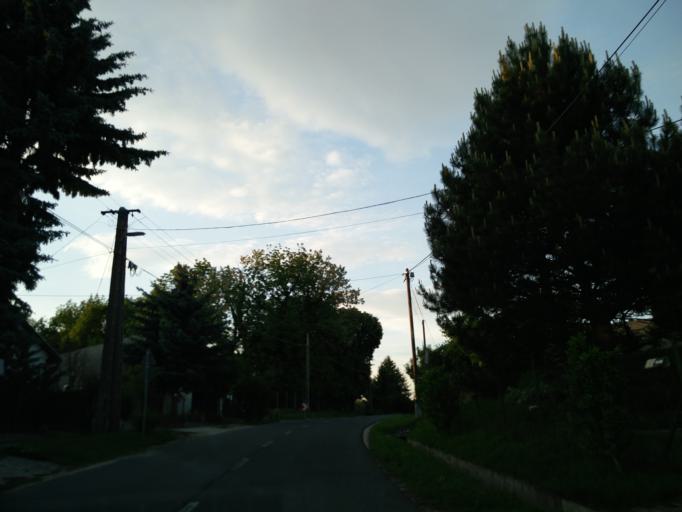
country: HU
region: Fejer
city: Bicske
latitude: 47.4292
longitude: 18.6027
